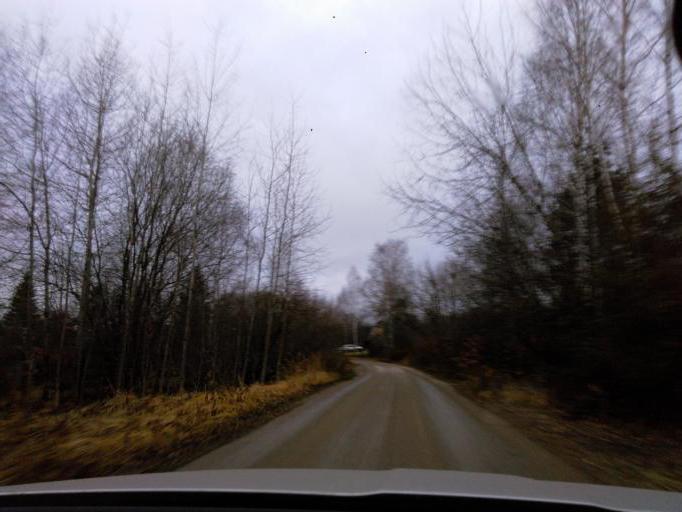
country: RU
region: Moskovskaya
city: Lozhki
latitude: 56.0588
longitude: 37.1051
